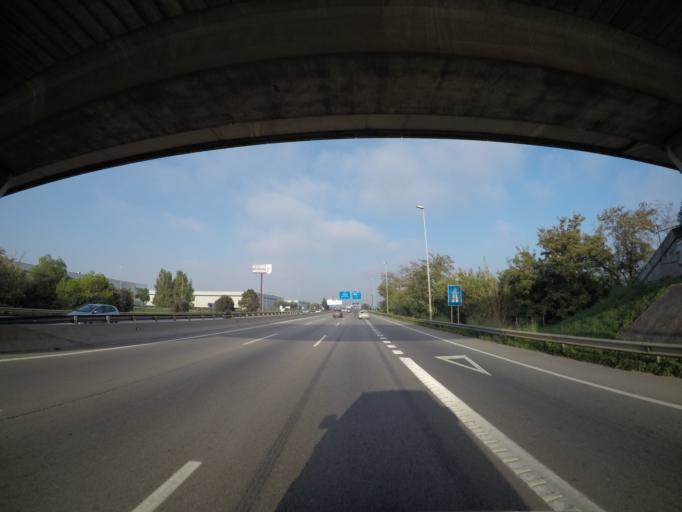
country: ES
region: Catalonia
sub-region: Provincia de Barcelona
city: Sant Boi de Llobregat
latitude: 41.3198
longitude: 2.0392
